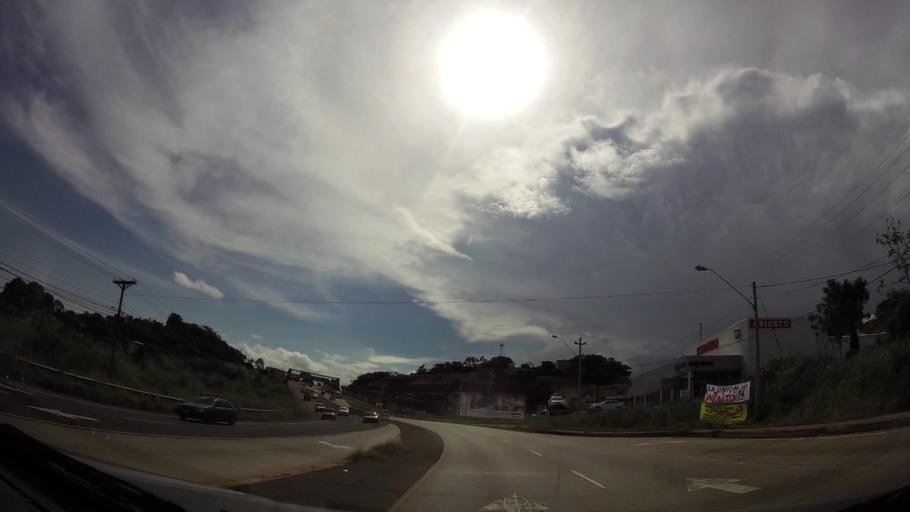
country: PA
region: Panama
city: La Chorrera
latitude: 8.8934
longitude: -79.7624
